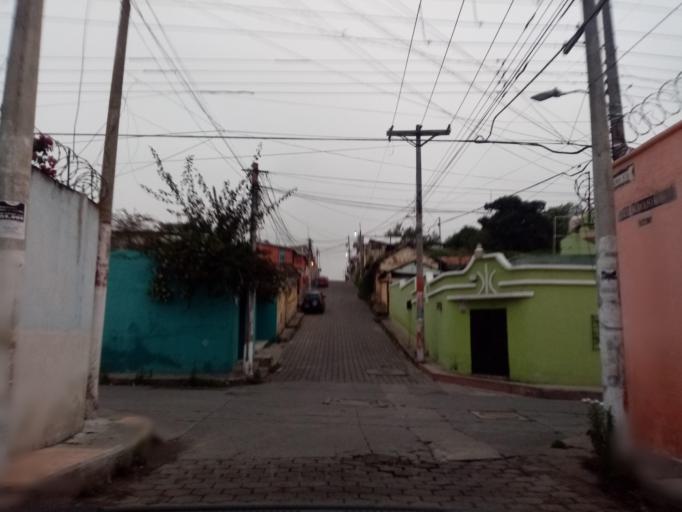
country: GT
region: Quetzaltenango
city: Quetzaltenango
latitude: 14.8395
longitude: -91.5146
